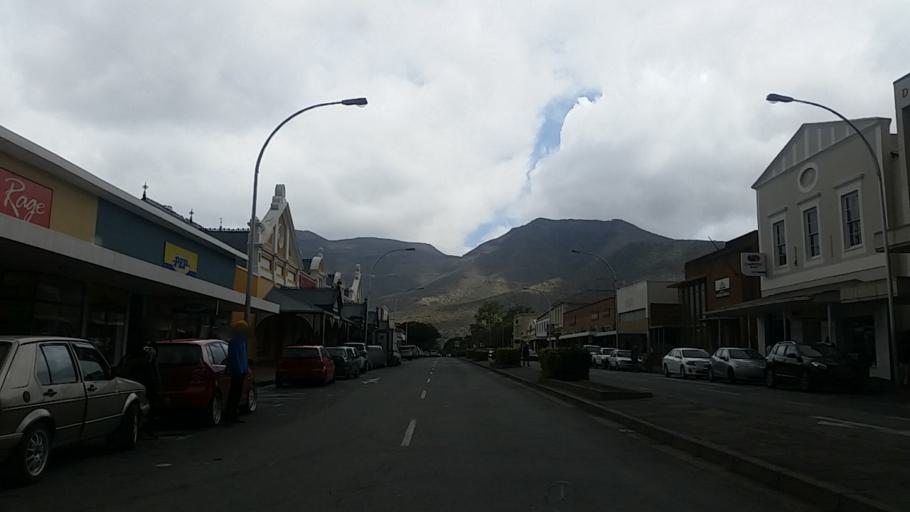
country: ZA
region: Eastern Cape
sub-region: Cacadu District Municipality
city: Graaff-Reinet
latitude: -32.2485
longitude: 24.5371
